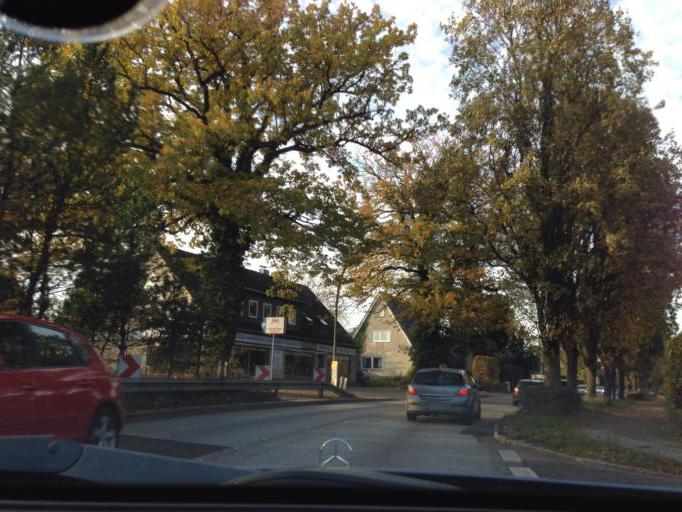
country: DE
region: Hamburg
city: Sasel
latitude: 53.6457
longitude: 10.1200
